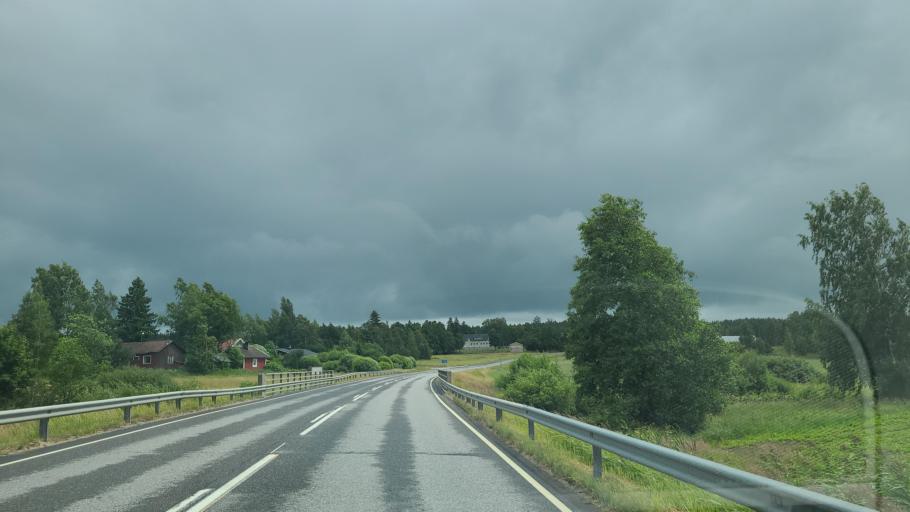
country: FI
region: Varsinais-Suomi
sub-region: Turku
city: Sauvo
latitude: 60.3323
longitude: 22.7103
